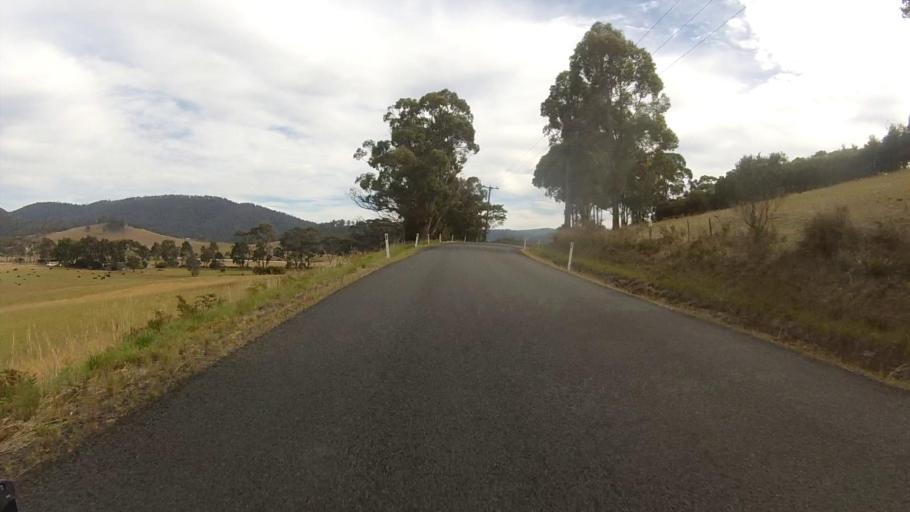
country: AU
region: Tasmania
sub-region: Sorell
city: Sorell
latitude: -42.7968
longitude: 147.7940
